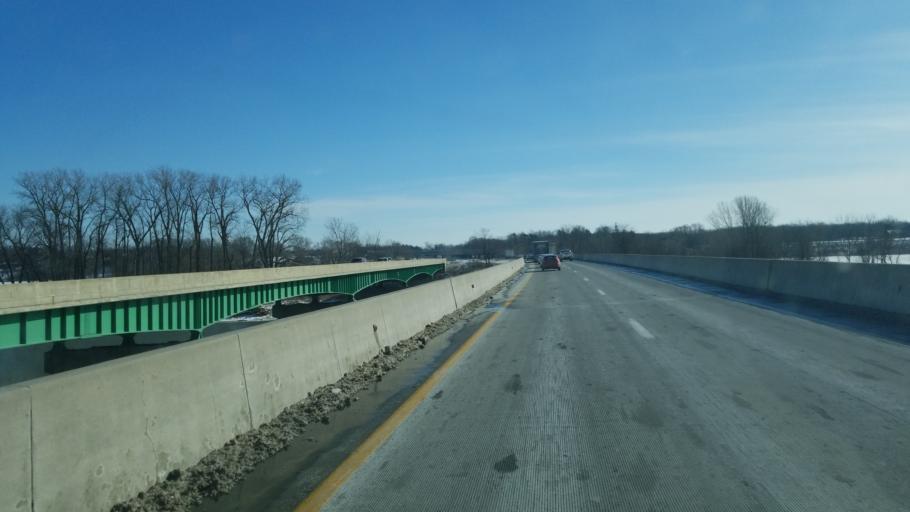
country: US
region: Ohio
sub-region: Lucas County
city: Maumee
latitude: 41.5462
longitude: -83.6833
